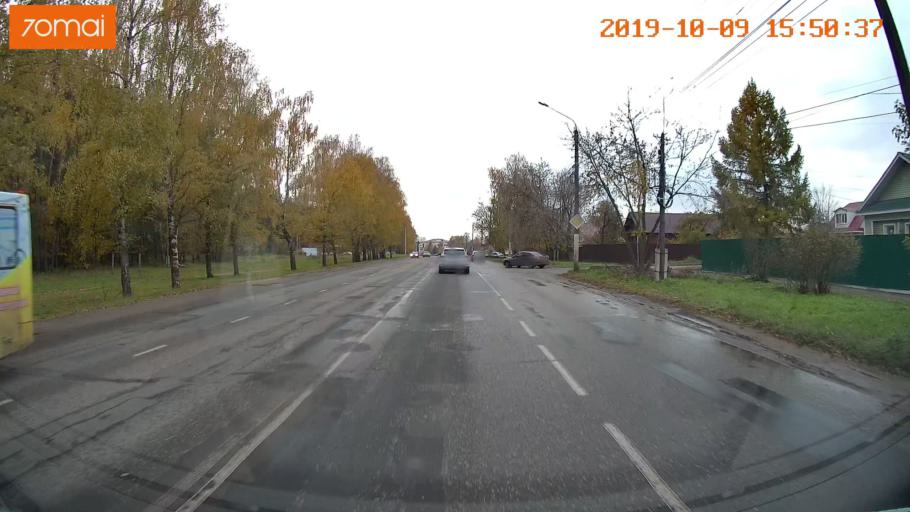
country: RU
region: Kostroma
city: Oktyabr'skiy
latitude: 57.8022
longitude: 40.9881
